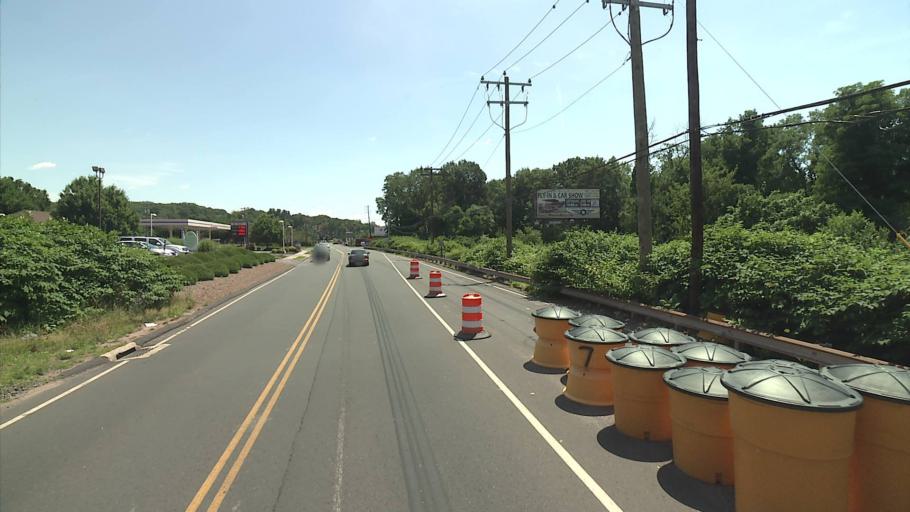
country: US
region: Connecticut
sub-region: Hartford County
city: Plainville
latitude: 41.6685
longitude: -72.8207
